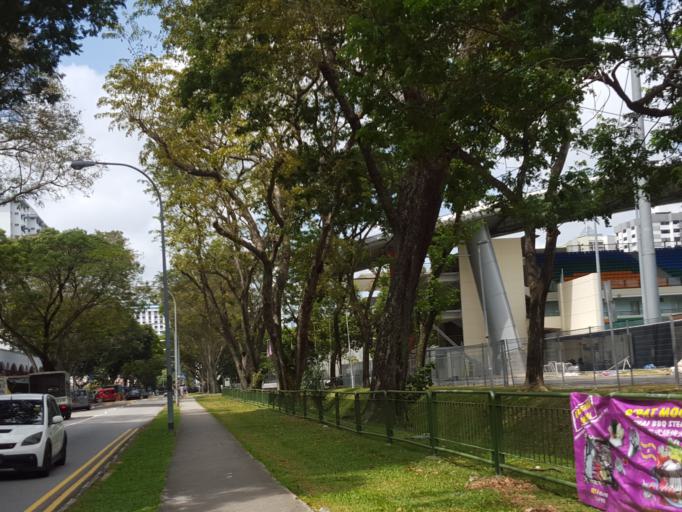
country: SG
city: Singapore
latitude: 1.3095
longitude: 103.8613
